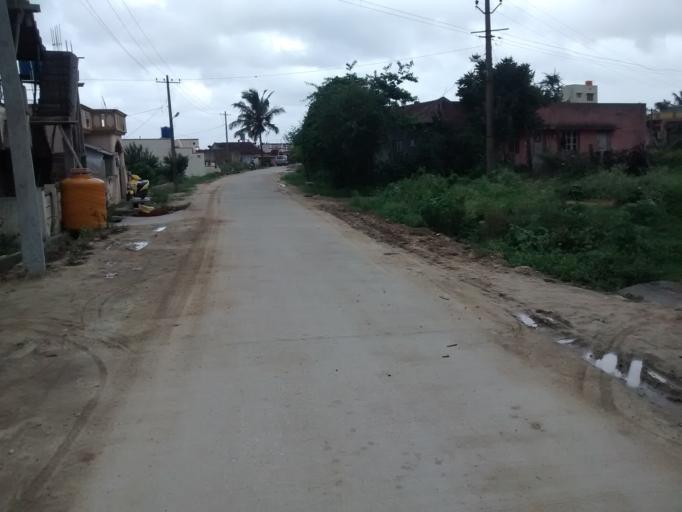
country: IN
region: Karnataka
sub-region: Hassan
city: Hassan
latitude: 12.9544
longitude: 76.1292
